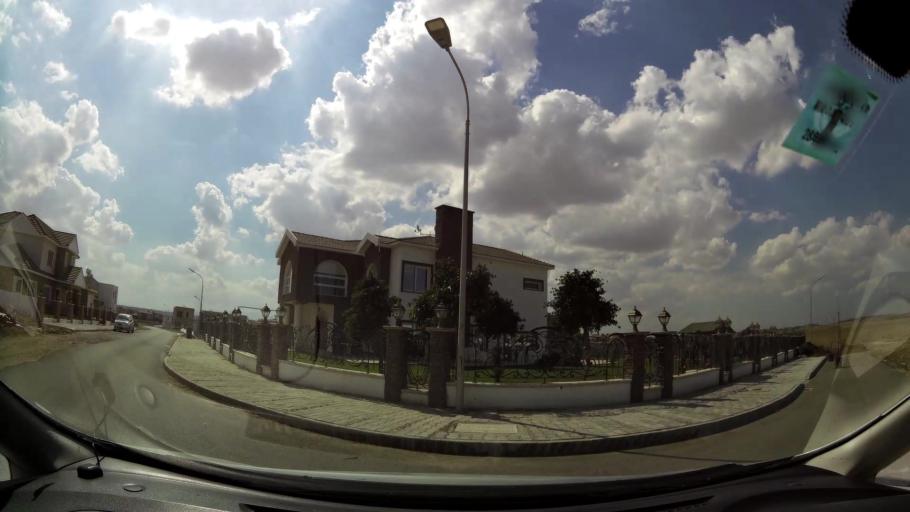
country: CY
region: Lefkosia
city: Nicosia
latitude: 35.2168
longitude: 33.2920
